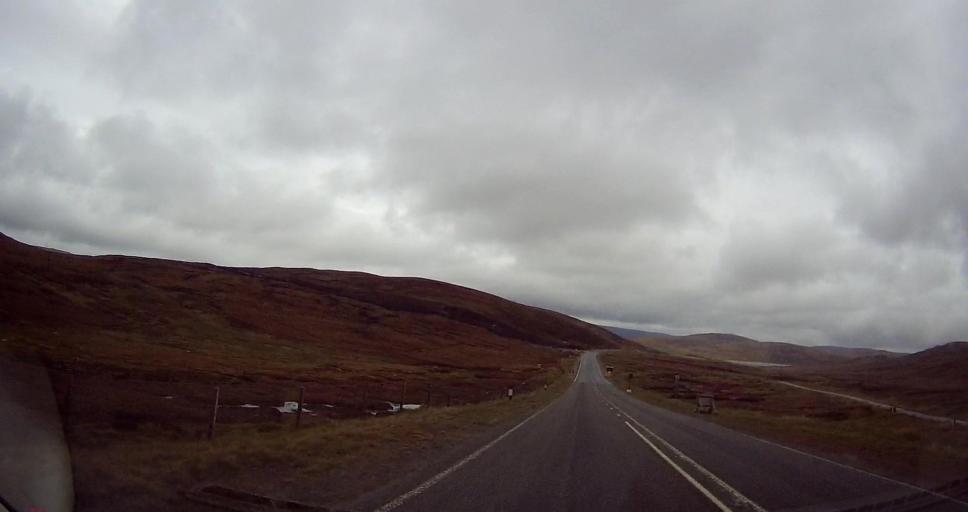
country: GB
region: Scotland
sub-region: Shetland Islands
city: Lerwick
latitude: 60.3261
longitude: -1.2529
